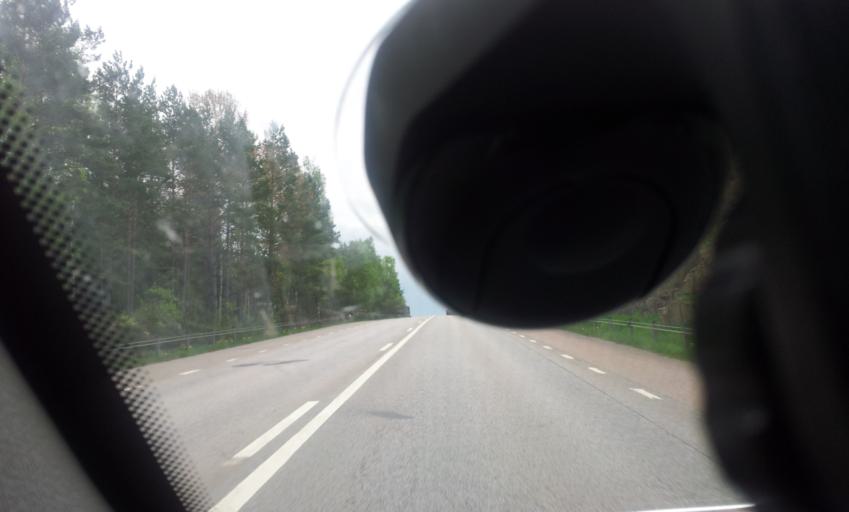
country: SE
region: Kalmar
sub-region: Vasterviks Kommun
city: Ankarsrum
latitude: 57.5956
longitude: 16.4826
